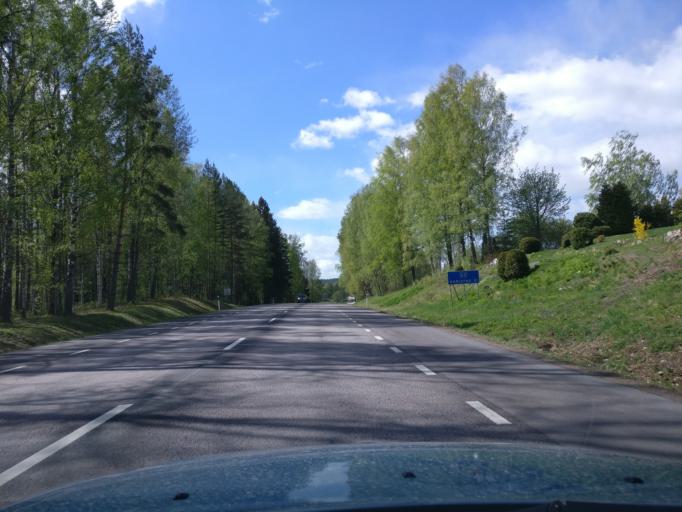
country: SE
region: Vaermland
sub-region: Karlstads Kommun
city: Molkom
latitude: 59.5971
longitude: 13.7134
